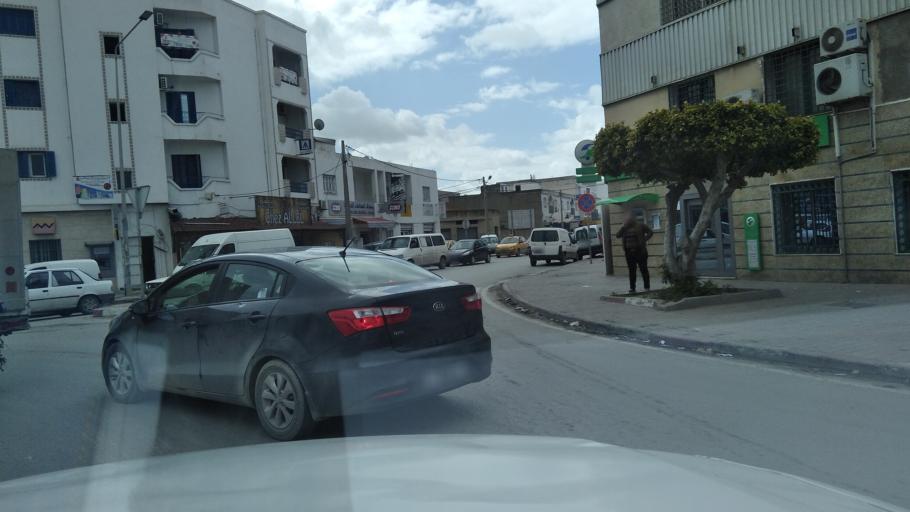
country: TN
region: Bin 'Arus
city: Ben Arous
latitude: 36.7640
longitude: 10.2265
